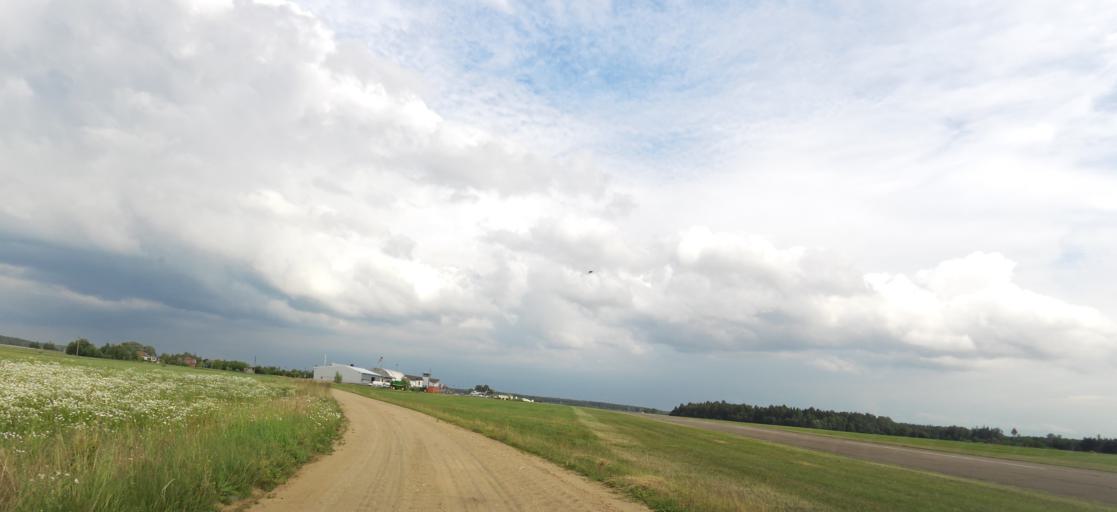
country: LT
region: Panevezys
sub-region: Panevezys City
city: Panevezys
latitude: 55.8292
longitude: 24.3548
